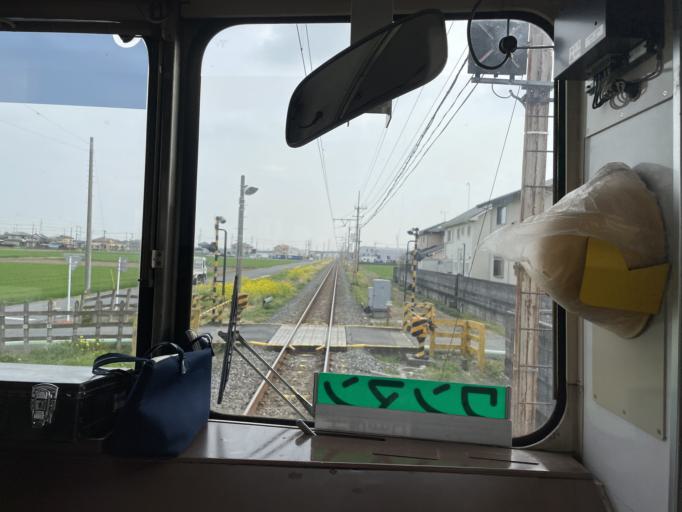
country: JP
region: Saitama
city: Kumagaya
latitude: 36.1363
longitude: 139.4096
